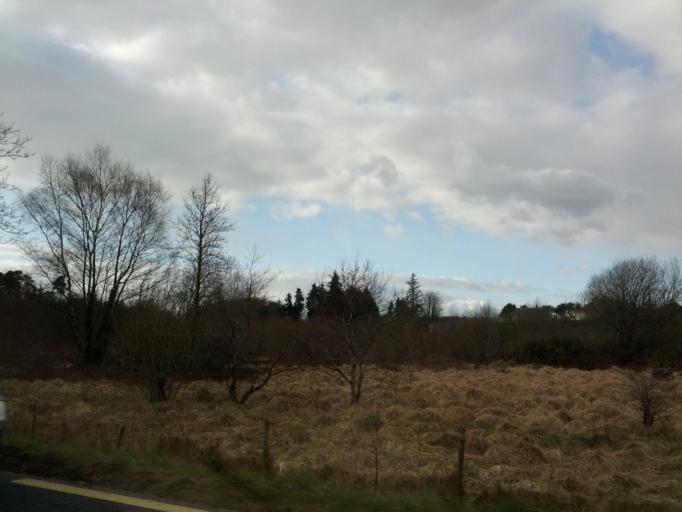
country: IE
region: Connaught
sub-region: County Galway
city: Athenry
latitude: 53.4549
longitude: -8.6892
